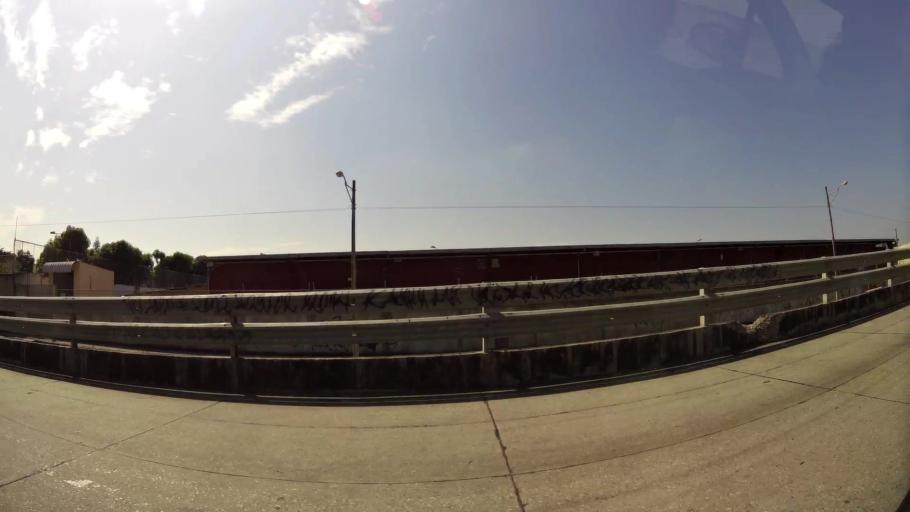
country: EC
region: Guayas
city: Eloy Alfaro
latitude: -2.1240
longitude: -79.9075
